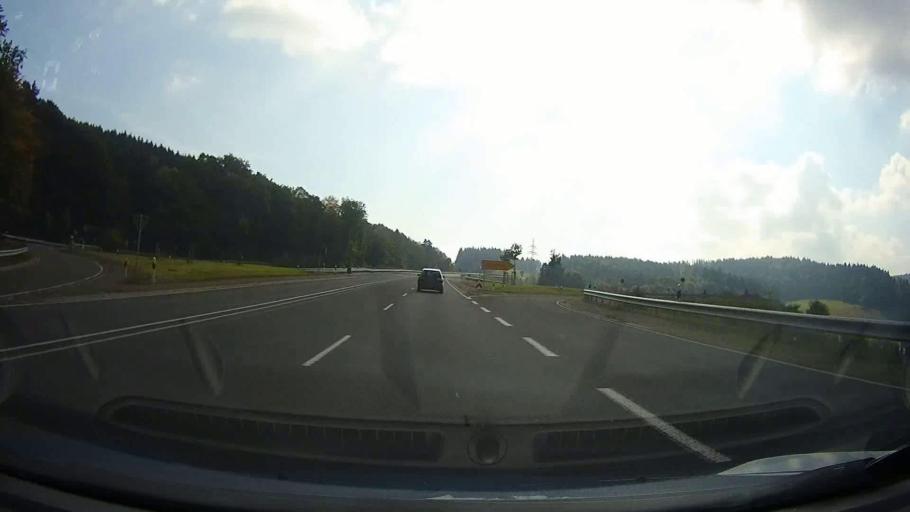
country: DE
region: Lower Saxony
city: Adelebsen
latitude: 51.6475
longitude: 9.7646
